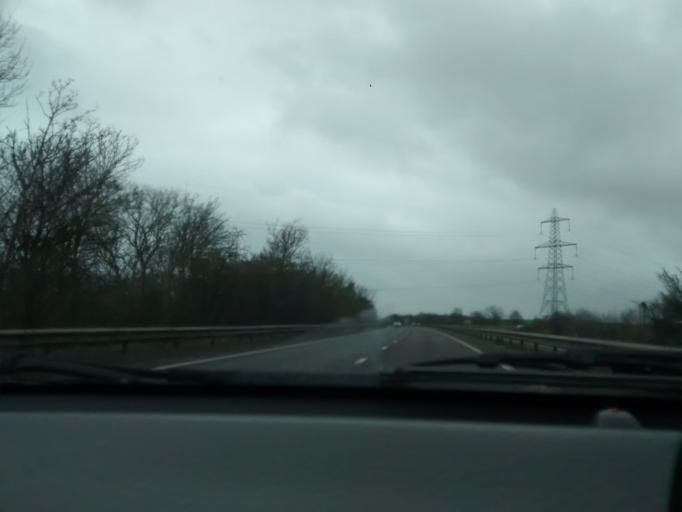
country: GB
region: England
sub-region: Suffolk
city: Needham Market
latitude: 52.1474
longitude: 1.0783
